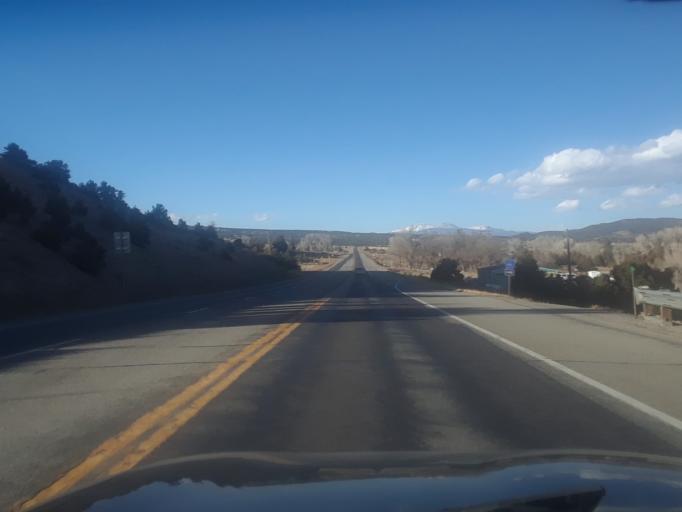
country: US
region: Colorado
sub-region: Chaffee County
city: Salida
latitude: 38.5723
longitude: -106.0805
